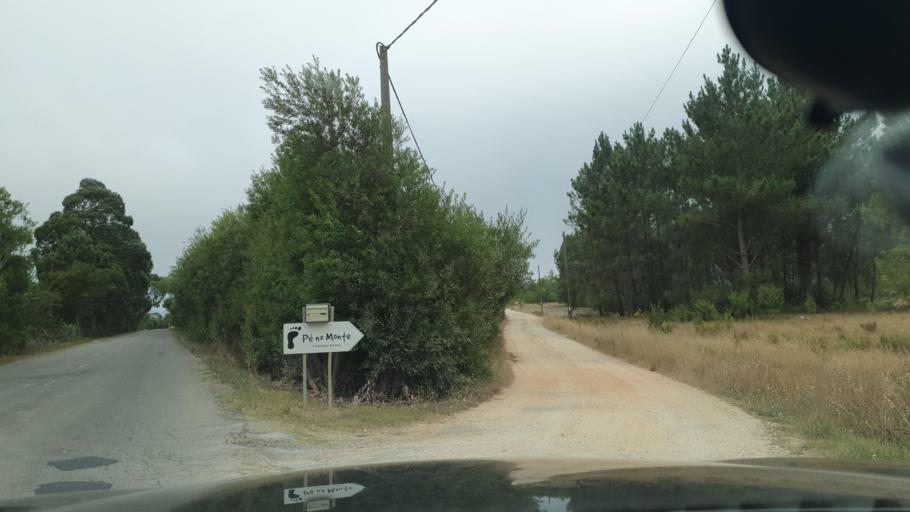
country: PT
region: Beja
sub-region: Odemira
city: Sao Teotonio
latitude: 37.4982
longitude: -8.6826
